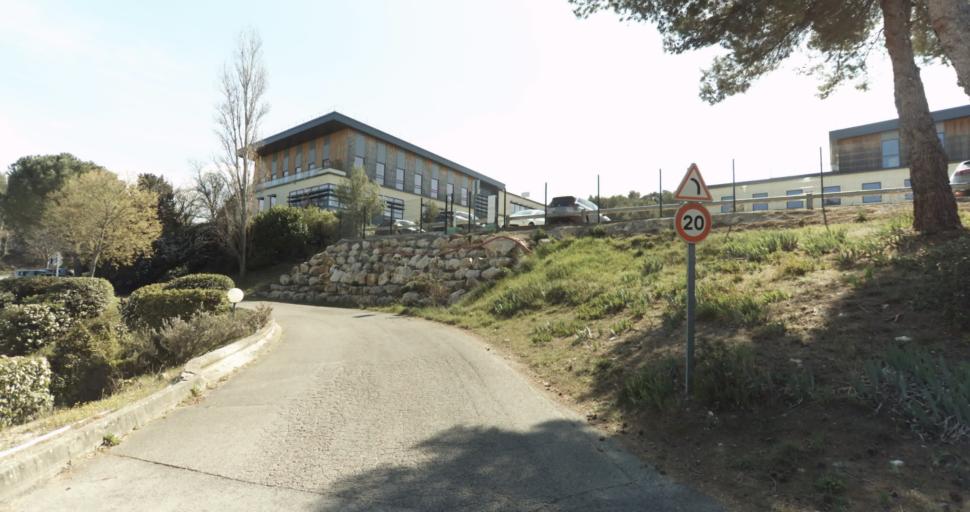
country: FR
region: Provence-Alpes-Cote d'Azur
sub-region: Departement des Bouches-du-Rhone
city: Cabries
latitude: 43.4754
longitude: 5.3755
